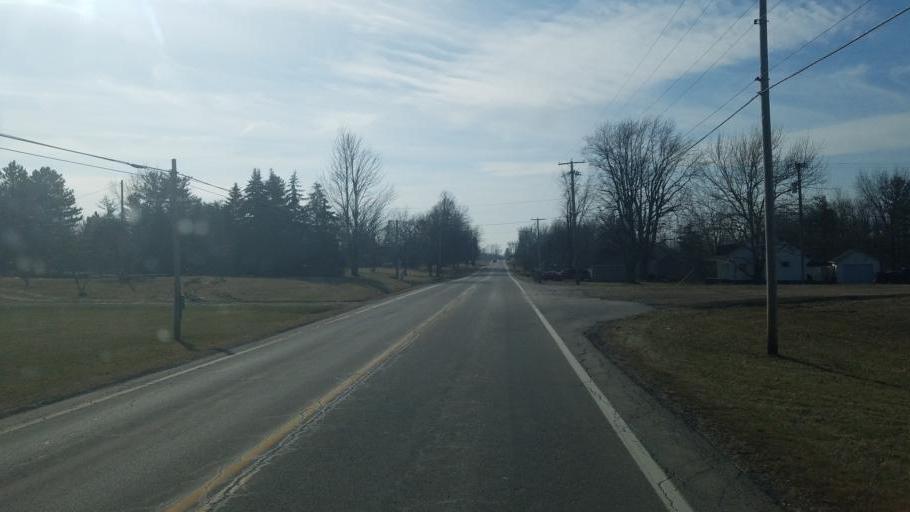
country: US
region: Ohio
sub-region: Crawford County
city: Crestline
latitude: 40.7640
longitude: -82.6821
